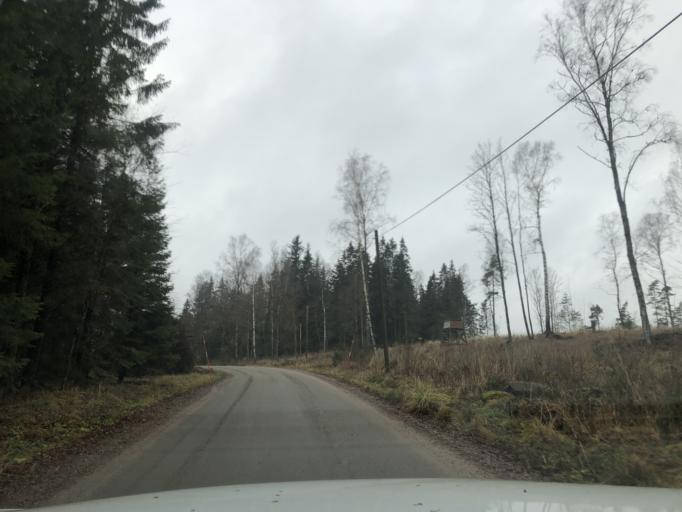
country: SE
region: Vaestra Goetaland
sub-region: Ulricehamns Kommun
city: Ulricehamn
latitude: 57.8588
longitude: 13.6159
